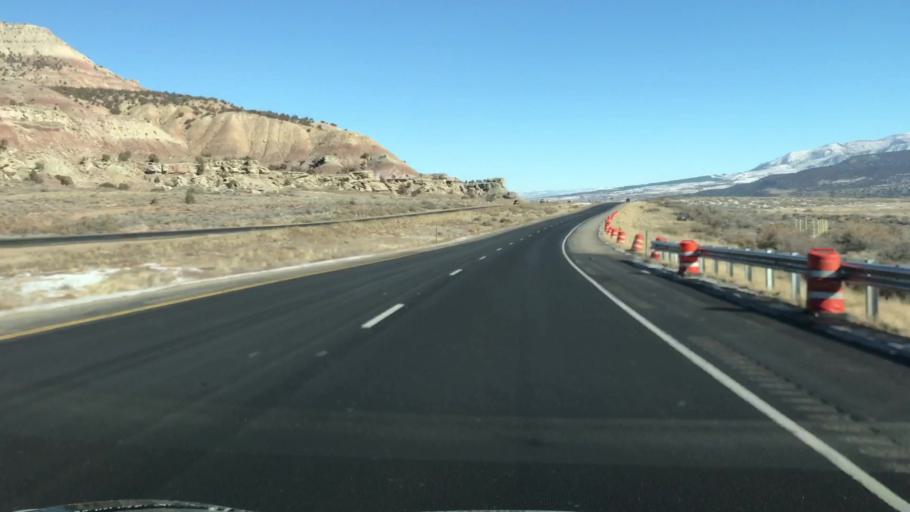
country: US
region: Colorado
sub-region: Garfield County
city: Parachute
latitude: 39.3963
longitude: -108.1234
